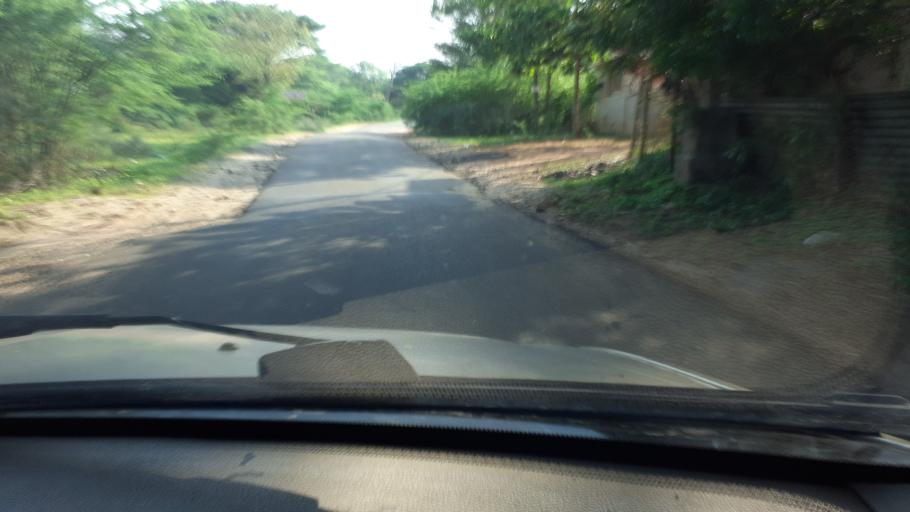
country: IN
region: Tamil Nadu
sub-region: Thoothukkudi
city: Eral
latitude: 8.5744
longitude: 78.0220
